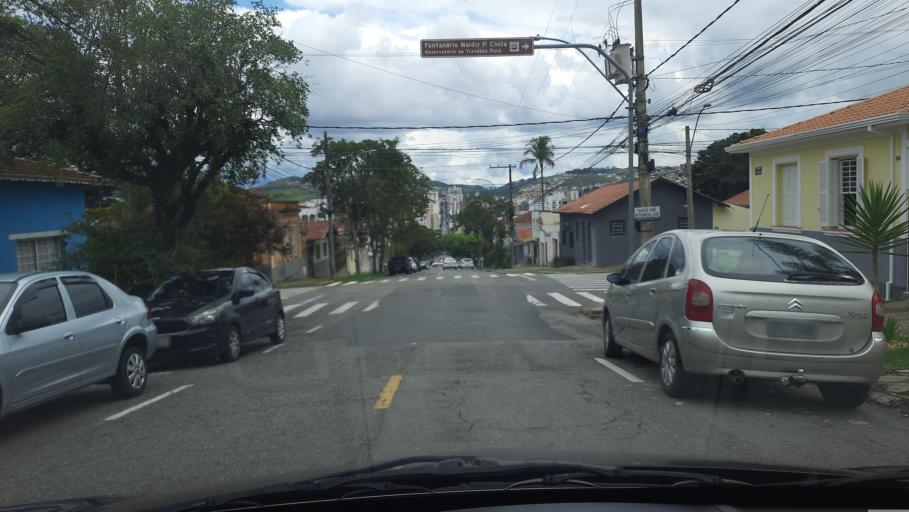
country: BR
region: Minas Gerais
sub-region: Pocos De Caldas
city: Pocos de Caldas
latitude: -21.7790
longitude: -46.5646
